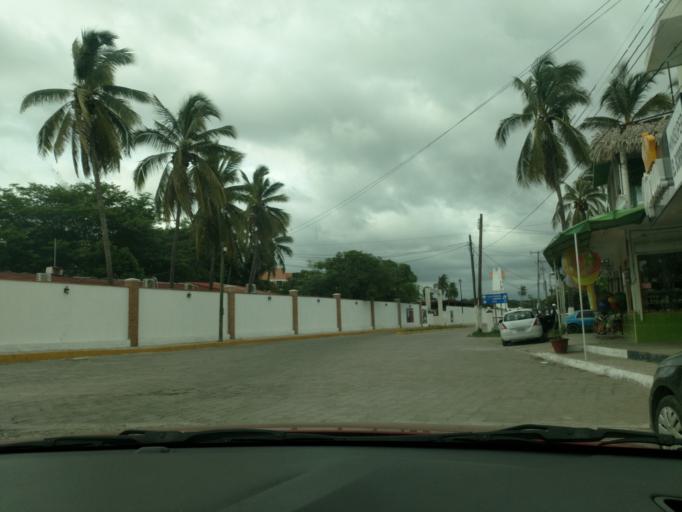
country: MX
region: Nayarit
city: San Blas
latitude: 21.5311
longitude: -105.2849
